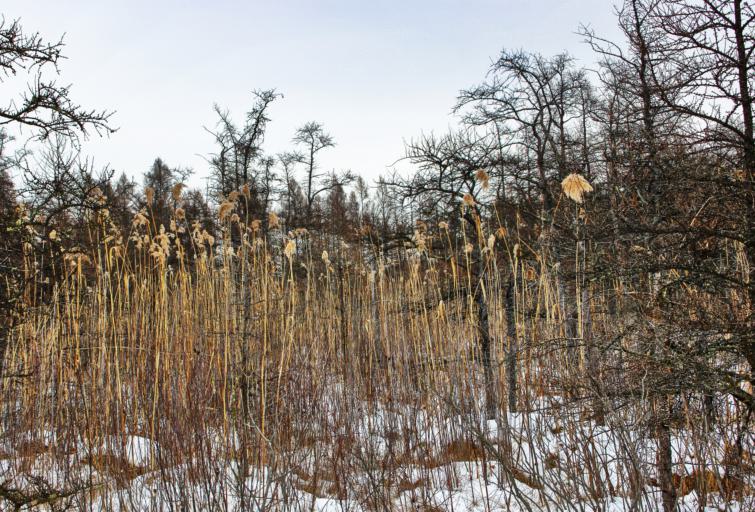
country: US
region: Wisconsin
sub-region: Dane County
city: Deerfield
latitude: 43.0904
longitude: -89.0382
